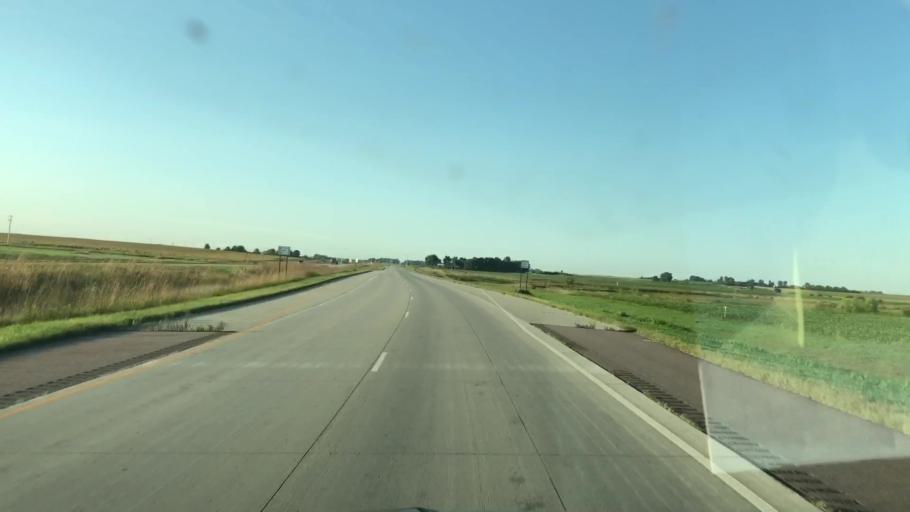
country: US
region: Minnesota
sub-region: Nobles County
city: Worthington
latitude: 43.5749
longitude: -95.6535
